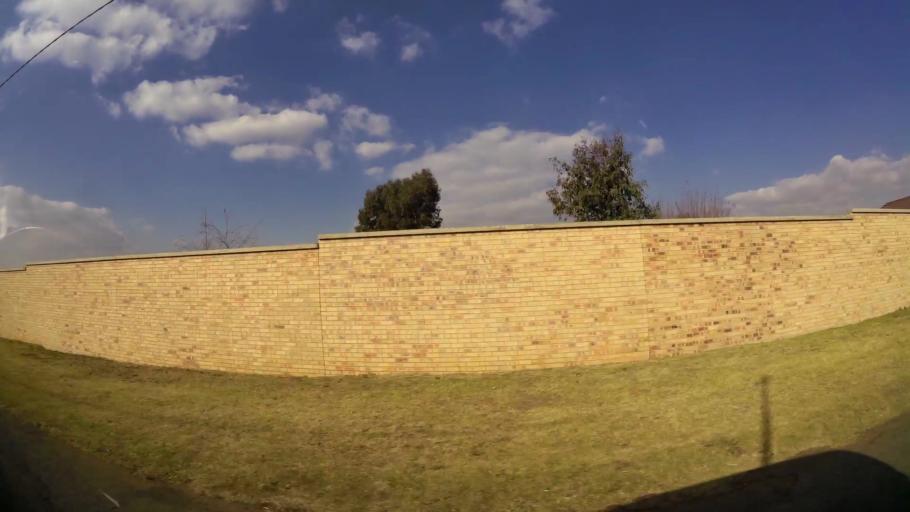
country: ZA
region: Gauteng
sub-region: West Rand District Municipality
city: Krugersdorp
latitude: -26.0901
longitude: 27.7447
